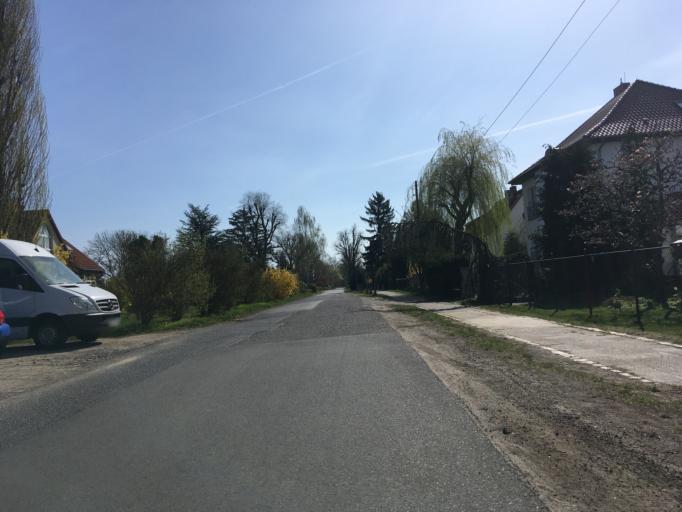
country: DE
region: Berlin
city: Kaulsdorf
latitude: 52.5071
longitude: 13.5986
